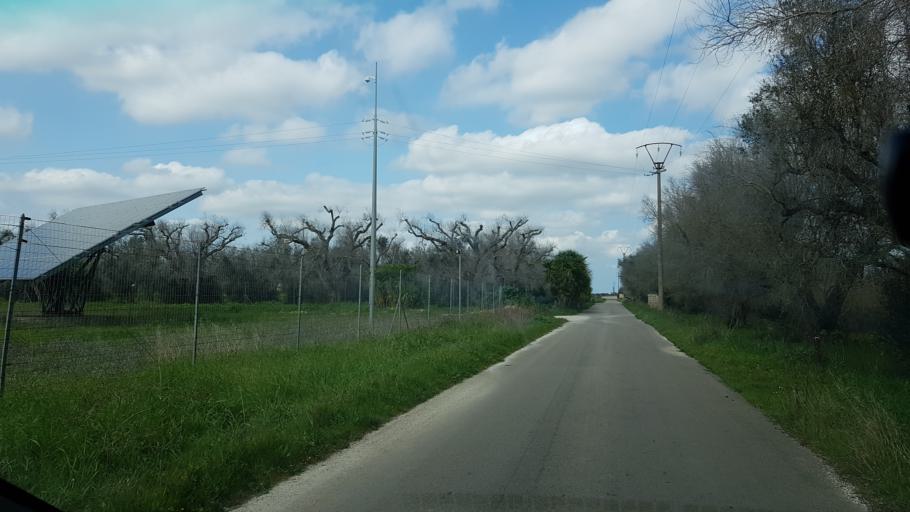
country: IT
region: Apulia
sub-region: Provincia di Brindisi
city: Torchiarolo
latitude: 40.4736
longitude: 18.0670
